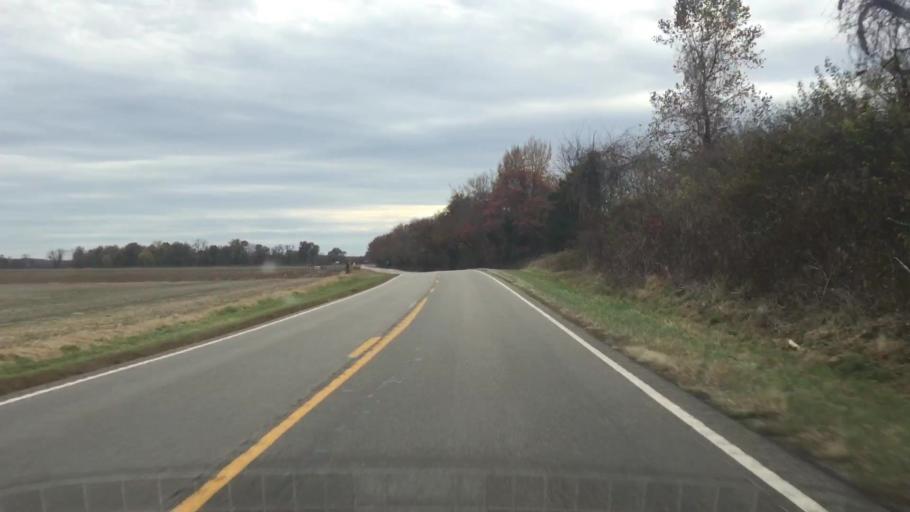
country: US
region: Missouri
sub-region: Callaway County
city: Holts Summit
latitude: 38.6082
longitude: -91.9859
